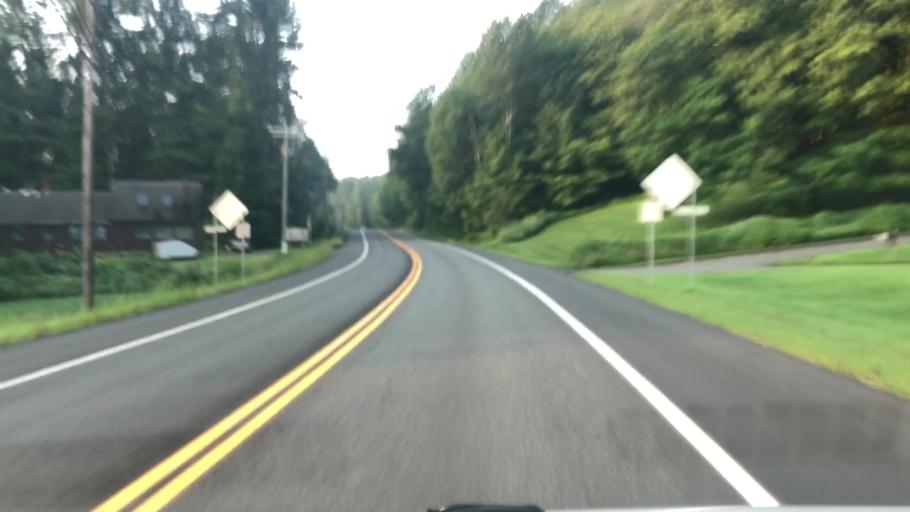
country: US
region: Massachusetts
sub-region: Franklin County
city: Shelburne
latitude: 42.6086
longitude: -72.6722
